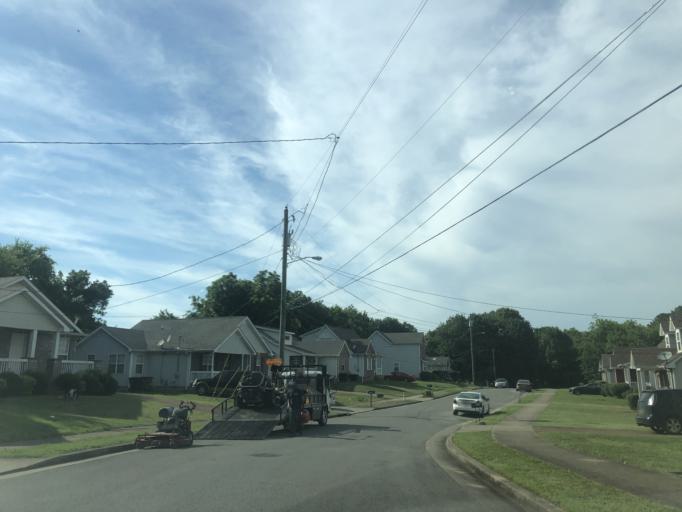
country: US
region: Tennessee
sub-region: Davidson County
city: Nashville
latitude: 36.2100
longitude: -86.8327
